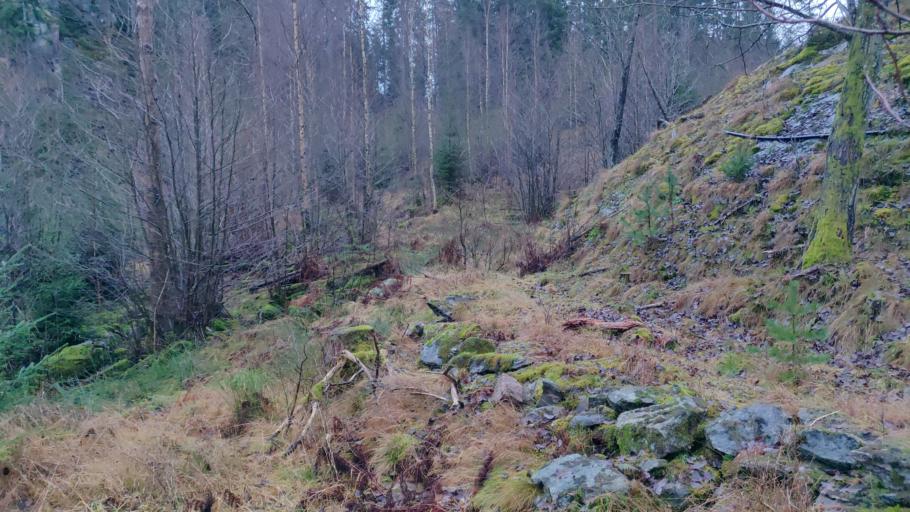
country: SE
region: Vaestra Goetaland
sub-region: Uddevalla Kommun
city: Uddevalla
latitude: 58.3429
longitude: 11.9832
